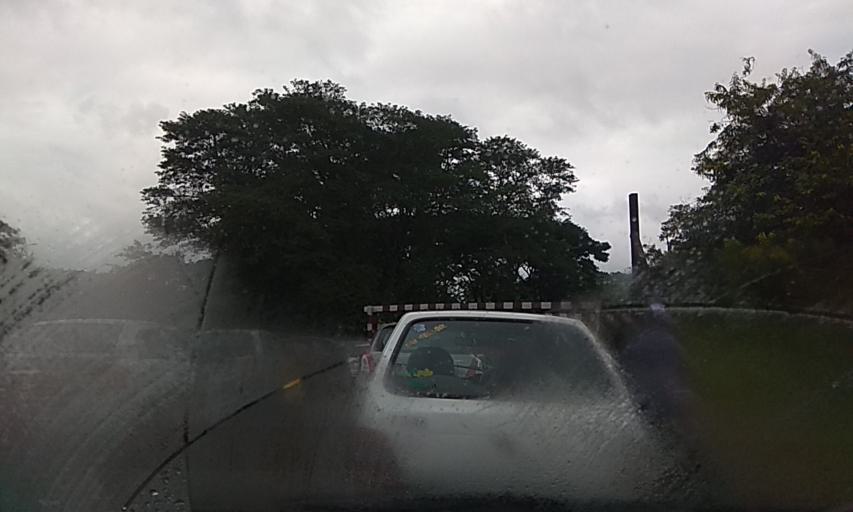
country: IN
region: Maharashtra
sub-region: Pune Division
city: Shivaji Nagar
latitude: 18.5462
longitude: 73.8472
